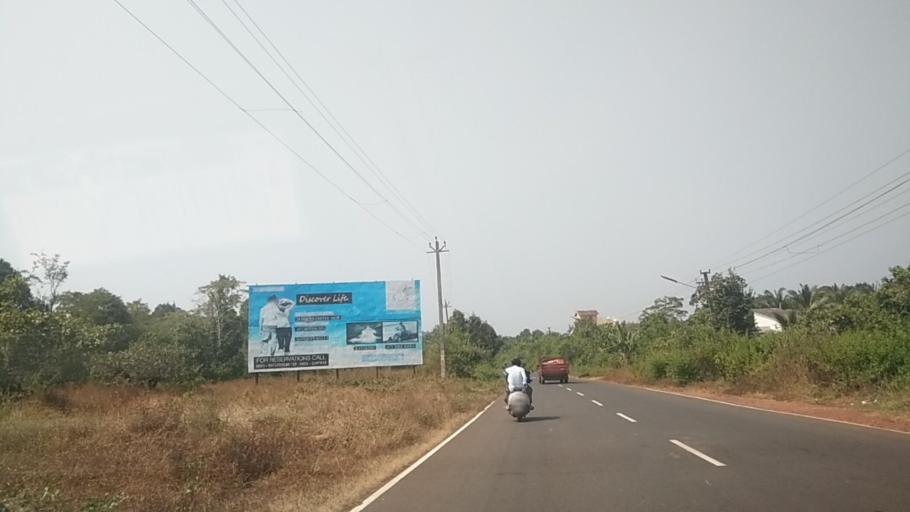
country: IN
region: Goa
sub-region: North Goa
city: Morjim
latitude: 15.6560
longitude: 73.7501
